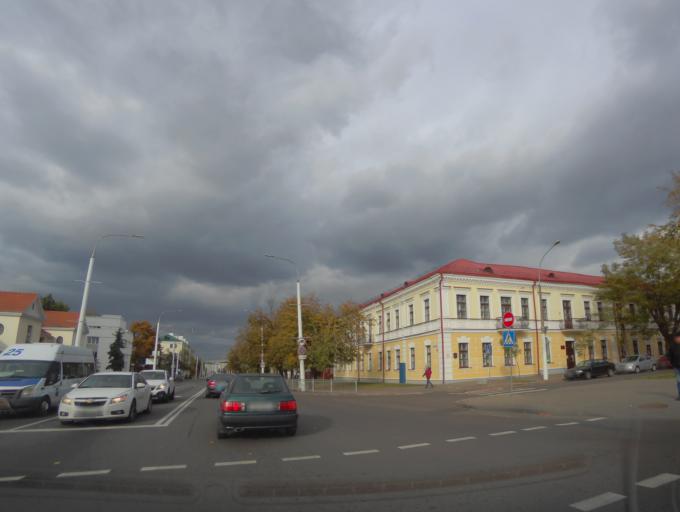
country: BY
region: Brest
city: Brest
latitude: 52.0861
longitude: 23.6866
